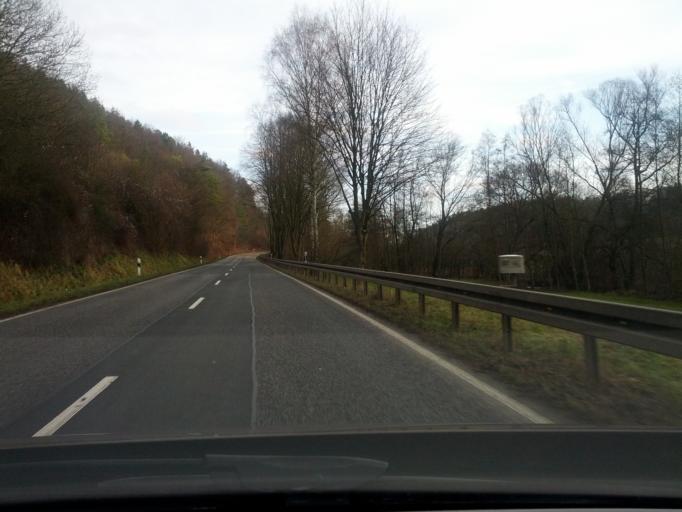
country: DE
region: Hesse
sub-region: Regierungsbezirk Kassel
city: Eschwege
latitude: 51.1154
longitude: 10.0385
